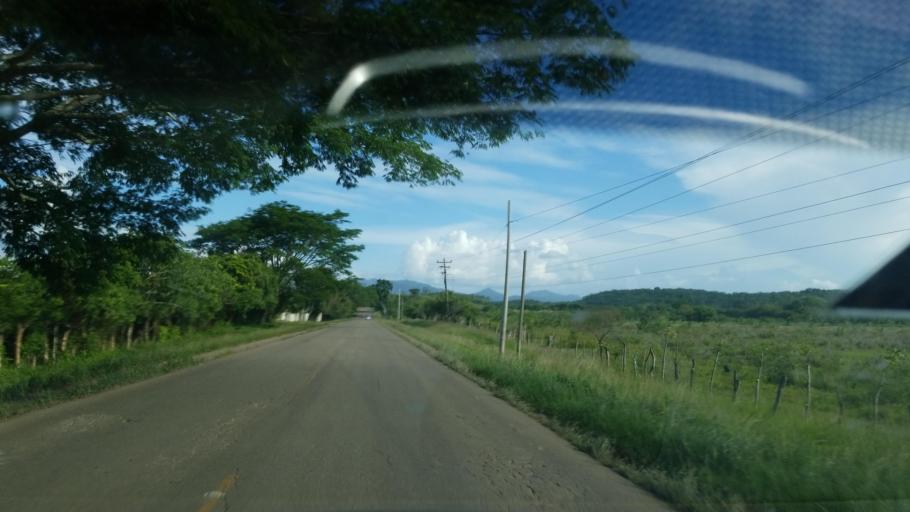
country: HN
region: El Paraiso
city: Arauli
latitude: 13.9333
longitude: -86.5583
